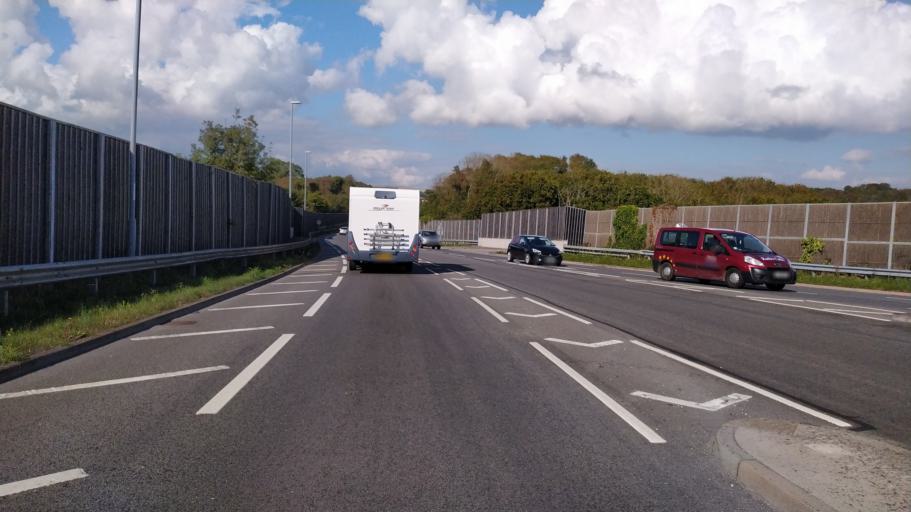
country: GB
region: England
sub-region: Dorset
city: Weymouth
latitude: 50.6358
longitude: -2.4627
